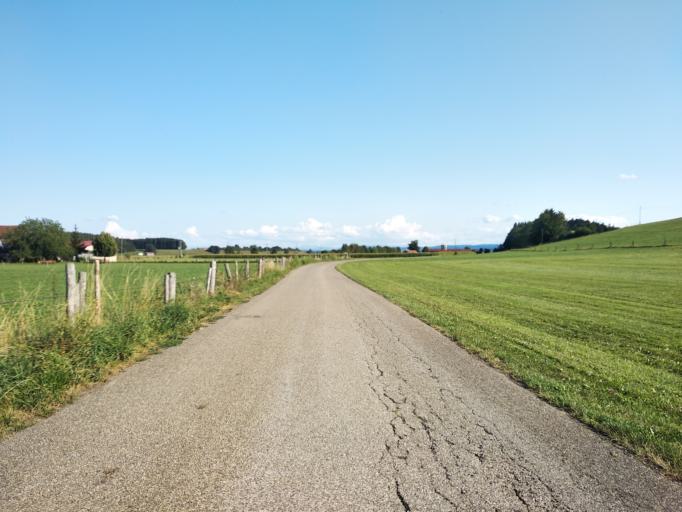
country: DE
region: Bavaria
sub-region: Swabia
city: Lautrach
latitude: 47.8856
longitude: 10.1148
